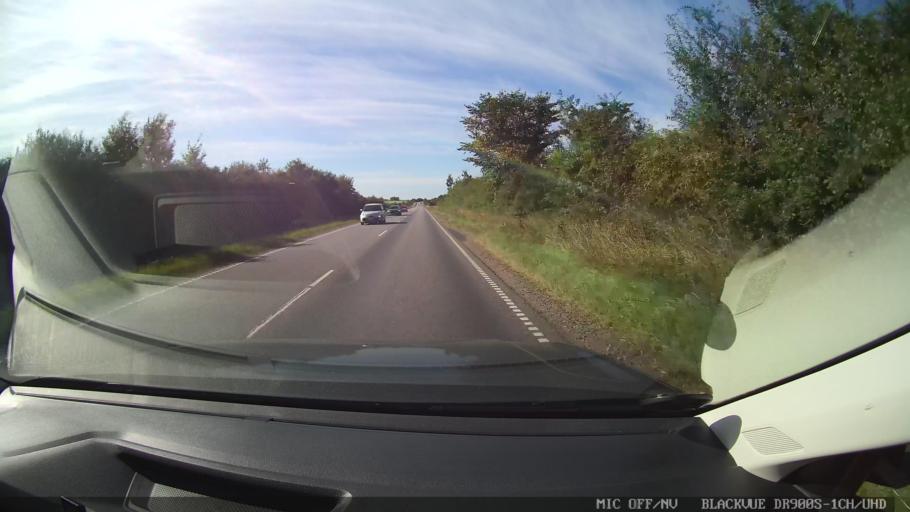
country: DK
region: North Denmark
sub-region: Mariagerfjord Kommune
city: Hobro
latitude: 56.6643
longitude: 9.8294
